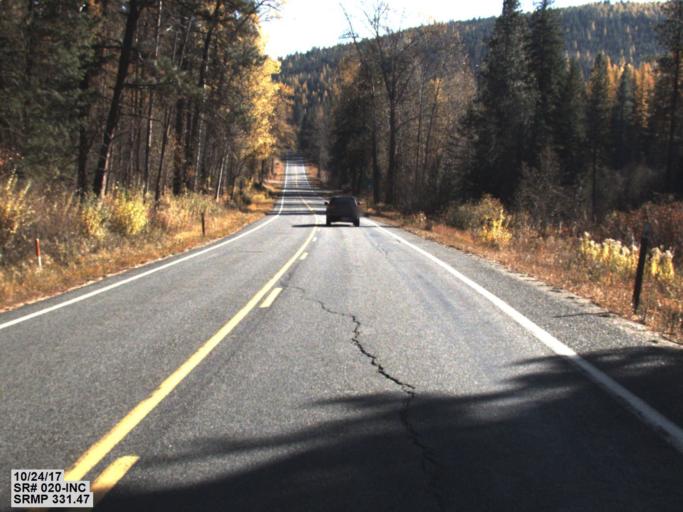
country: US
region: Washington
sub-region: Stevens County
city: Kettle Falls
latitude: 48.5832
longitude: -118.3021
